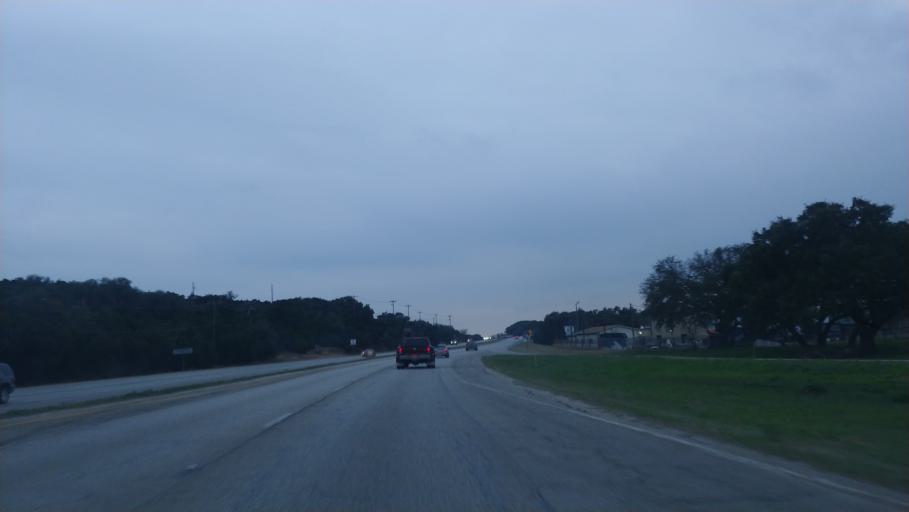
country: US
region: Texas
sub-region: Bexar County
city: Helotes
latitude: 29.5743
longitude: -98.6884
